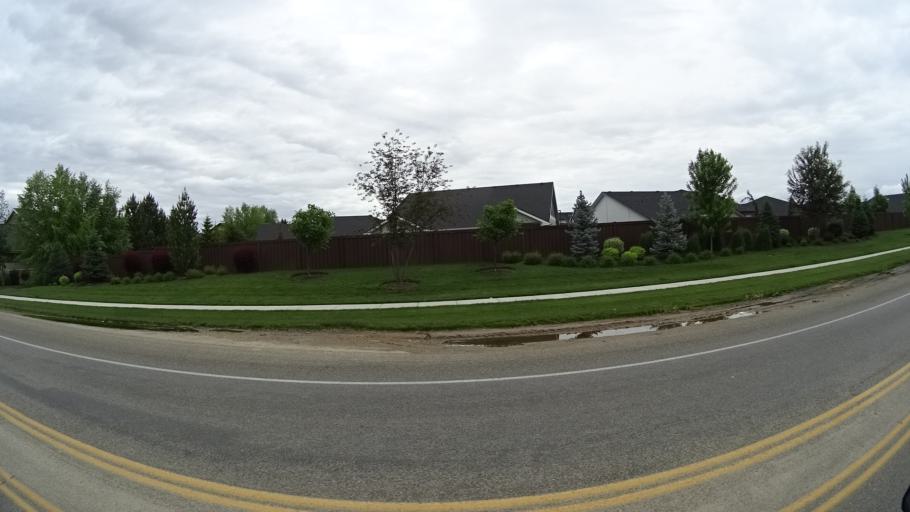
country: US
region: Idaho
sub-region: Ada County
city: Meridian
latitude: 43.6483
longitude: -116.4111
